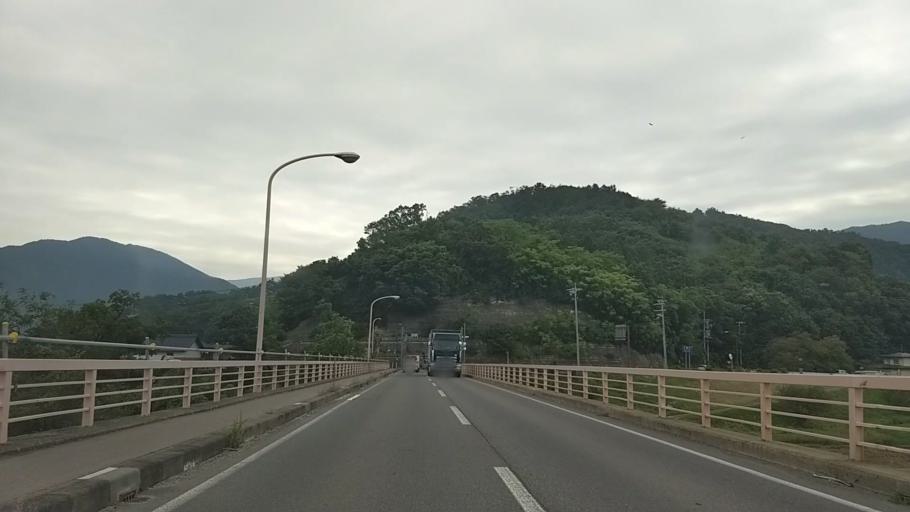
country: JP
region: Nagano
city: Nagano-shi
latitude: 36.6055
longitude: 138.2246
